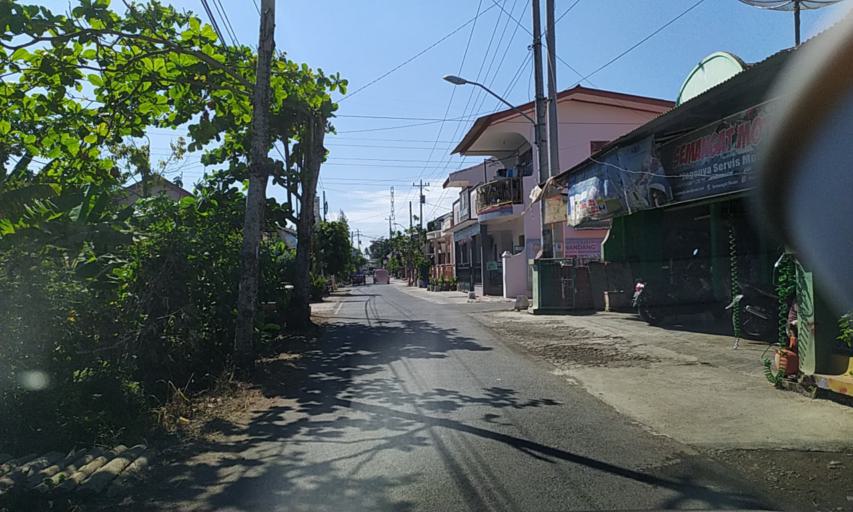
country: ID
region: Central Java
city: Rejanegara
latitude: -7.6889
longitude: 109.0348
